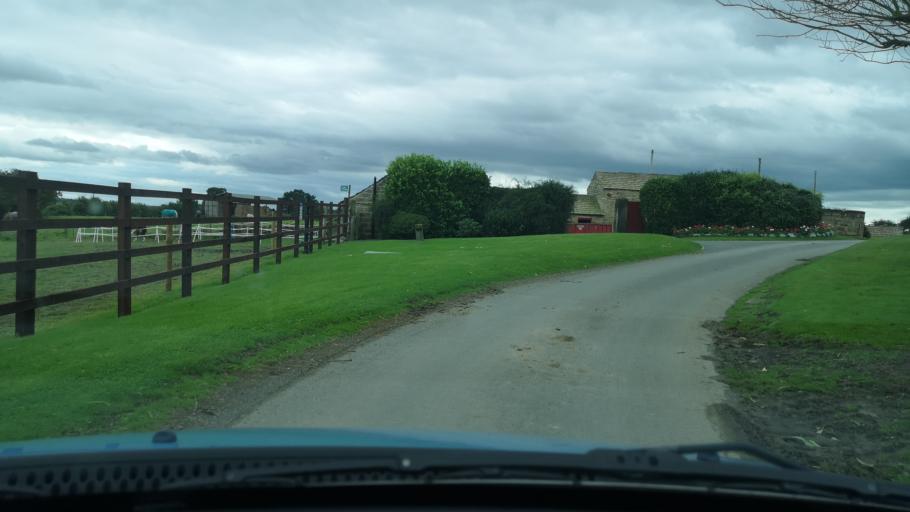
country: GB
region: England
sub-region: City and Borough of Wakefield
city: Featherstone
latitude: 53.6541
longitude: -1.3475
